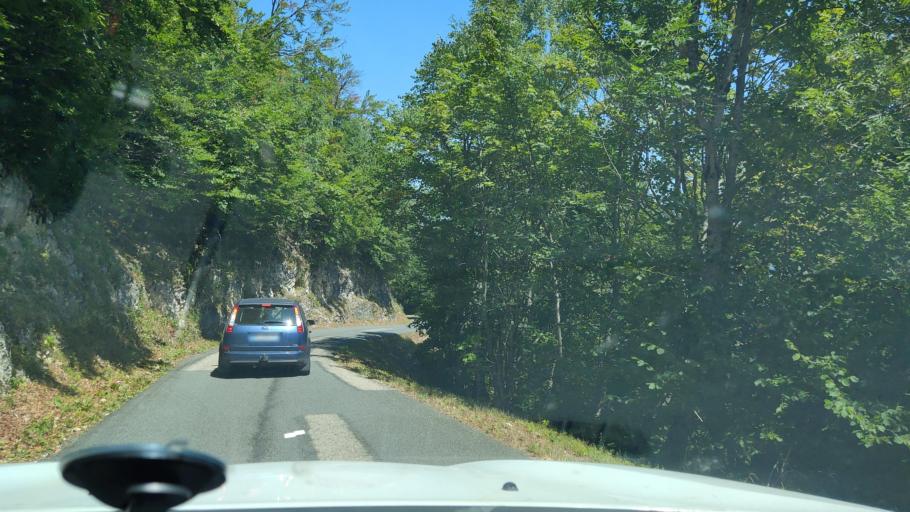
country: FR
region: Rhone-Alpes
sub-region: Departement de la Savoie
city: Le Bourget-du-Lac
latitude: 45.6522
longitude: 5.8289
